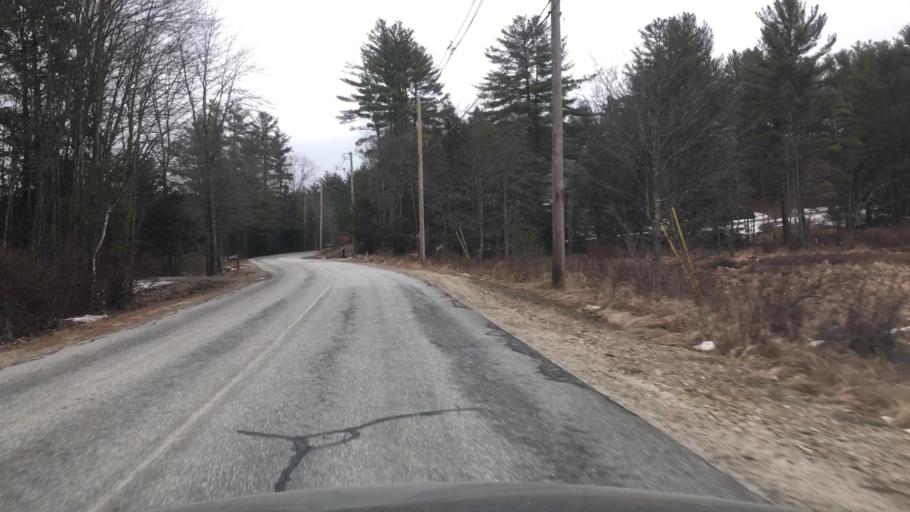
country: US
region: New Hampshire
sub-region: Hillsborough County
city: Goffstown
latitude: 42.9612
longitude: -71.6213
